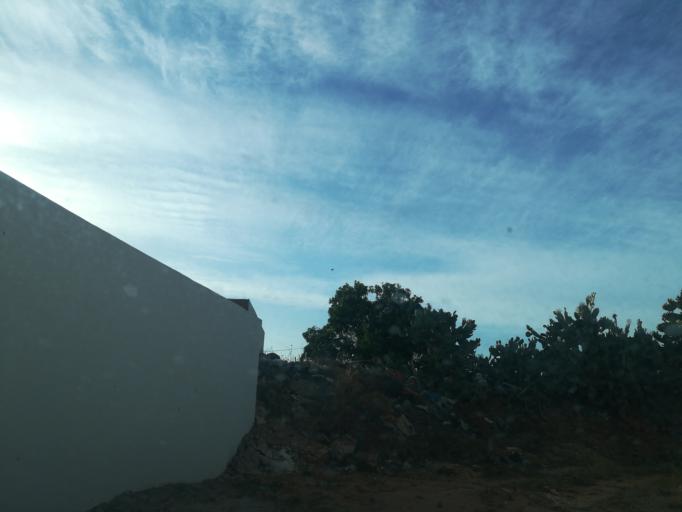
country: TN
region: Safaqis
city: Al Qarmadah
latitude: 34.8156
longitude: 10.7492
